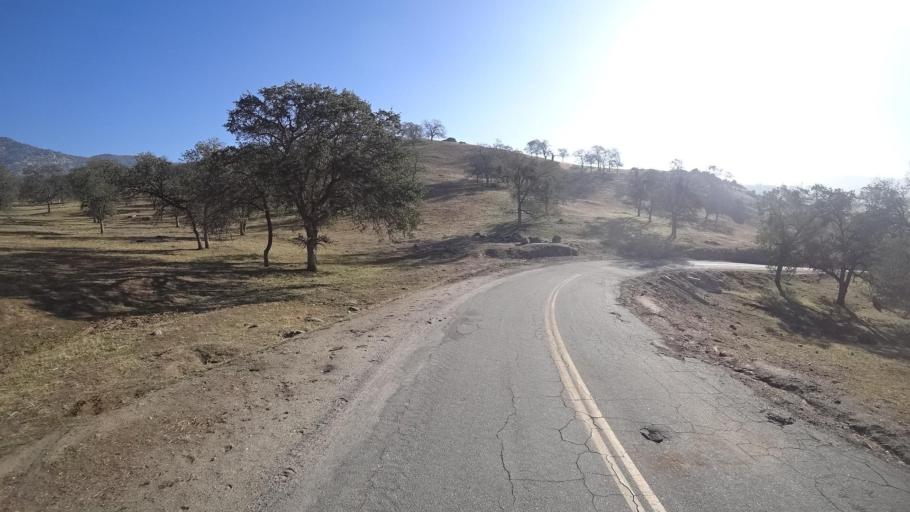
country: US
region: California
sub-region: Kern County
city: Alta Sierra
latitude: 35.7321
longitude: -118.8138
